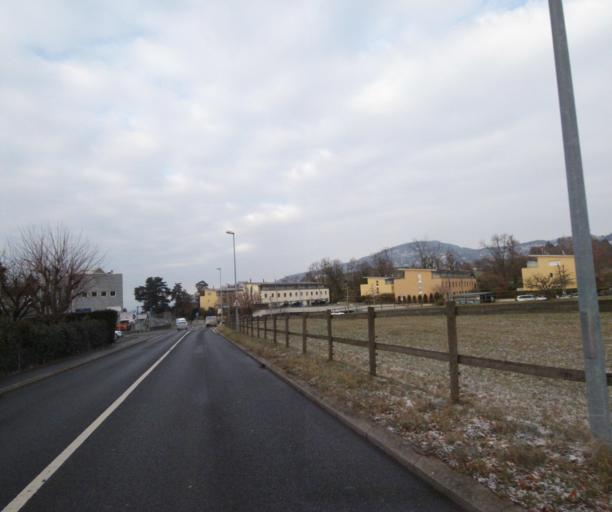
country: CH
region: Vaud
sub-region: Riviera-Pays-d'Enhaut District
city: La Tour-de-Peilz
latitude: 46.4613
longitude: 6.8699
